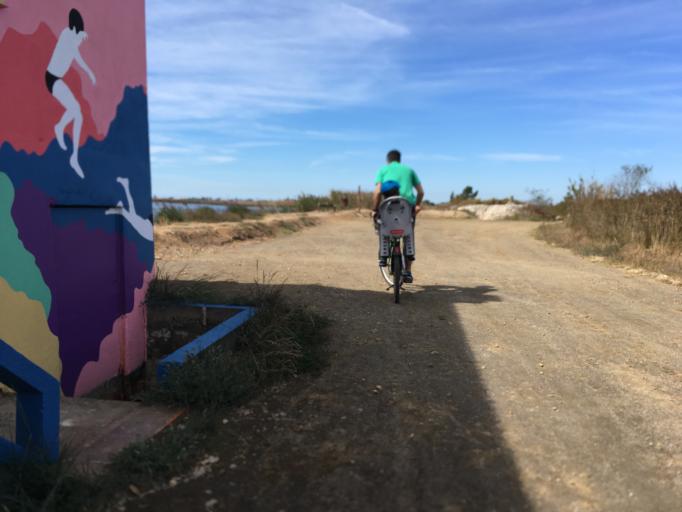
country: PT
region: Aveiro
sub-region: Murtosa
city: Murtosa
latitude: 40.7230
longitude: -8.5995
